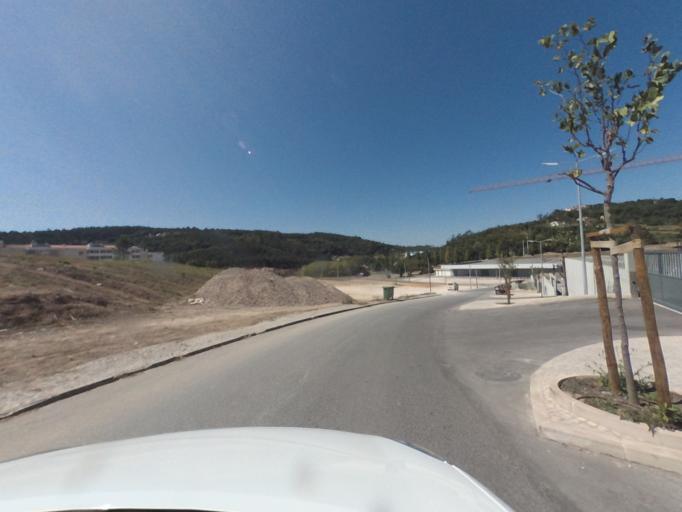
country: PT
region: Leiria
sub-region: Alcobaca
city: Alcobaca
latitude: 39.5566
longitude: -8.9781
